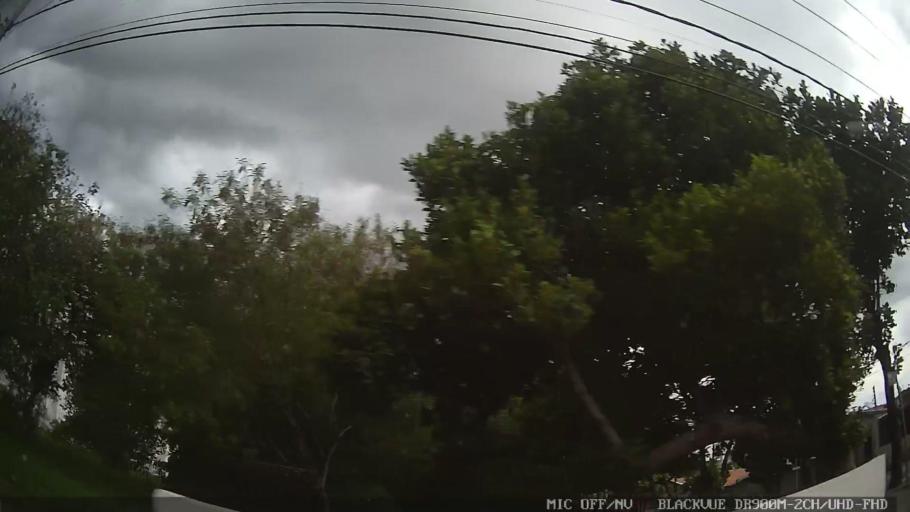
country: BR
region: Sao Paulo
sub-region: Amparo
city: Amparo
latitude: -22.7132
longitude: -46.7908
